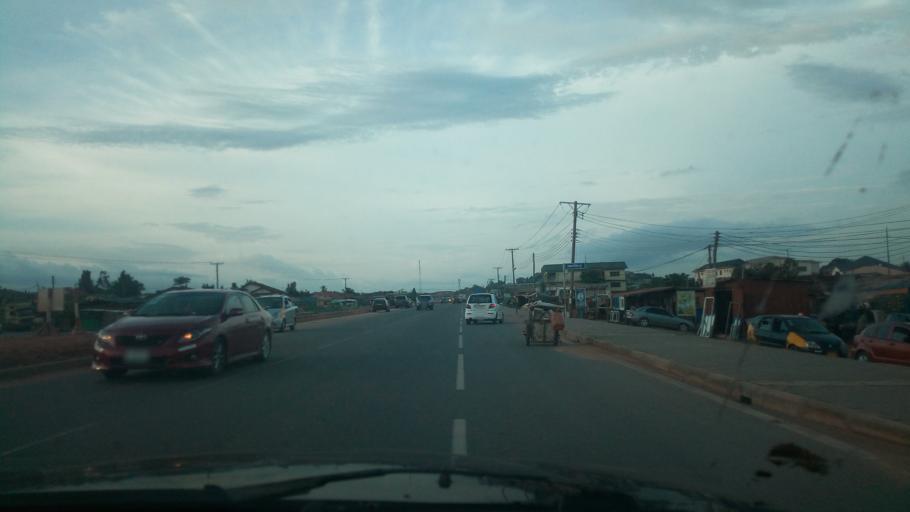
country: GH
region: Western
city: Takoradi
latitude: 4.9269
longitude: -1.7823
